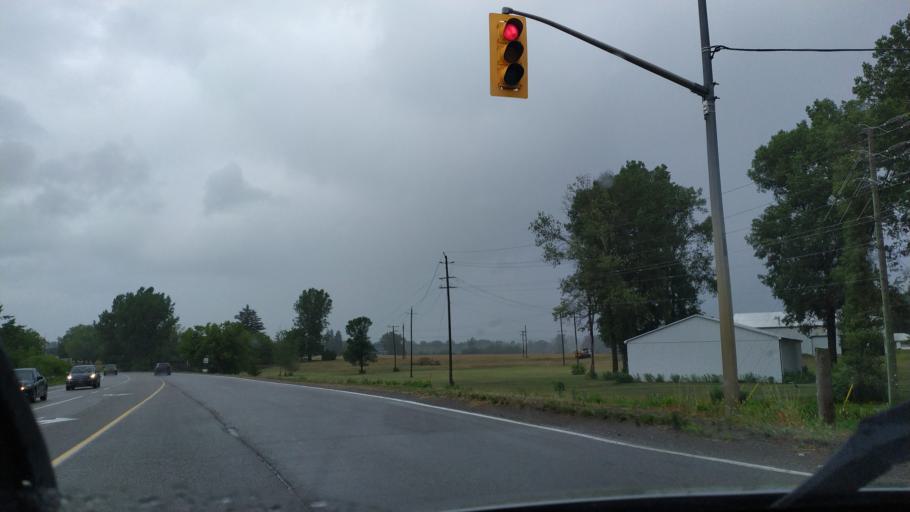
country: CA
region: Ontario
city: Quinte West
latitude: 44.1082
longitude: -77.6205
